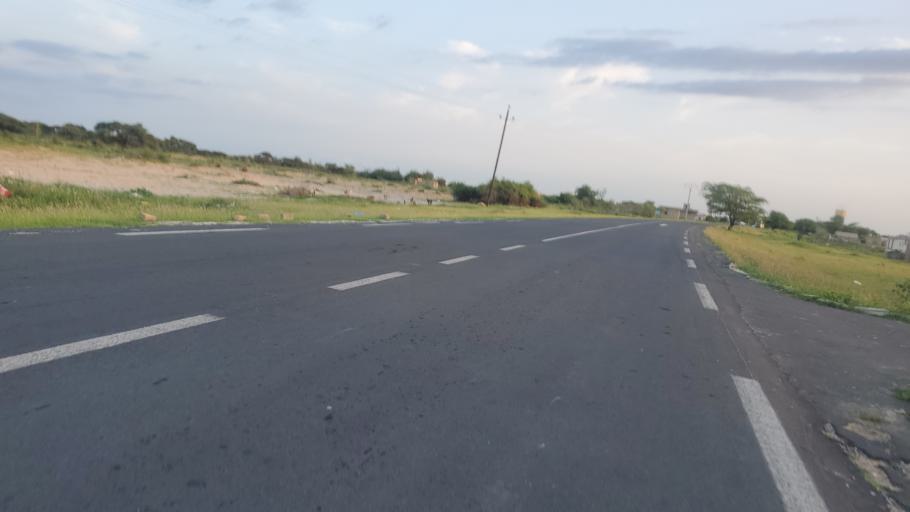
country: SN
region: Saint-Louis
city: Saint-Louis
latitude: 16.1406
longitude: -16.4098
